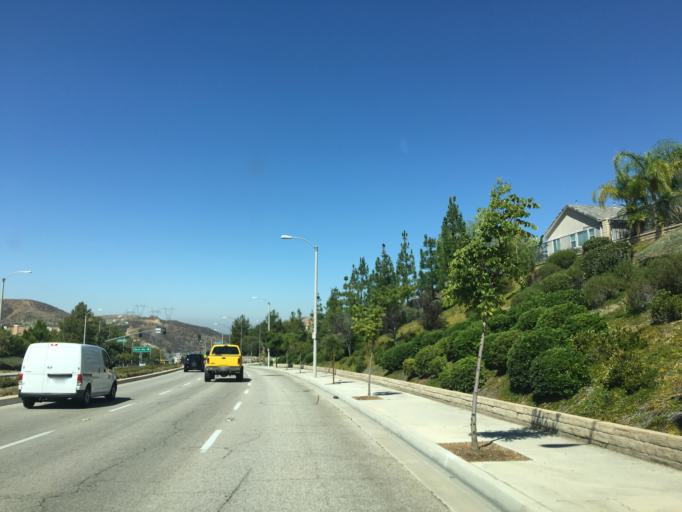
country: US
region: California
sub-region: Los Angeles County
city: Santa Clarita
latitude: 34.4471
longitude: -118.4792
